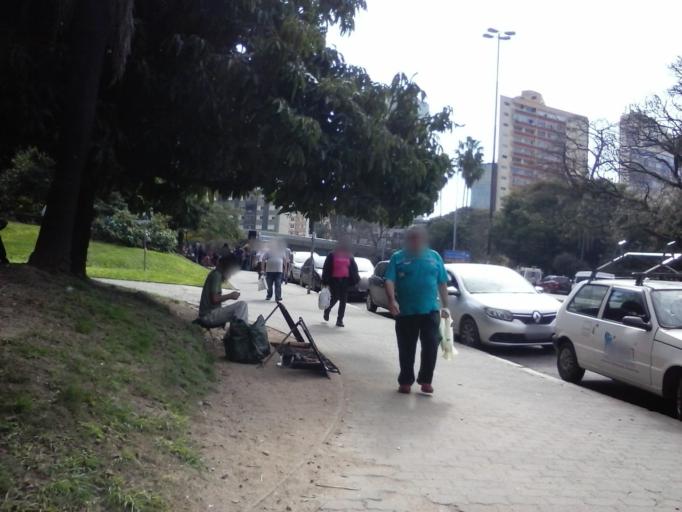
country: BR
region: Rio Grande do Sul
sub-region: Porto Alegre
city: Porto Alegre
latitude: -30.0325
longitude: -51.2235
